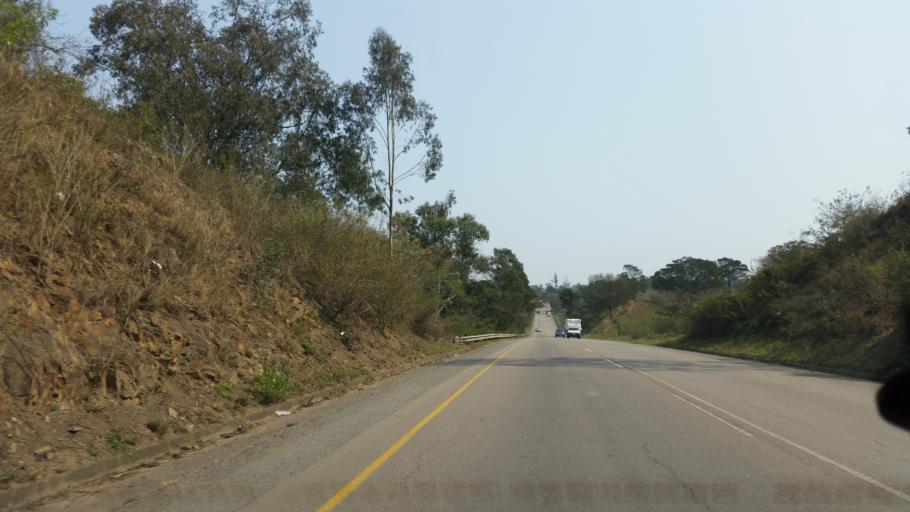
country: ZA
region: KwaZulu-Natal
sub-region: eThekwini Metropolitan Municipality
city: Mpumalanga
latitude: -29.7361
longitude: 30.6556
